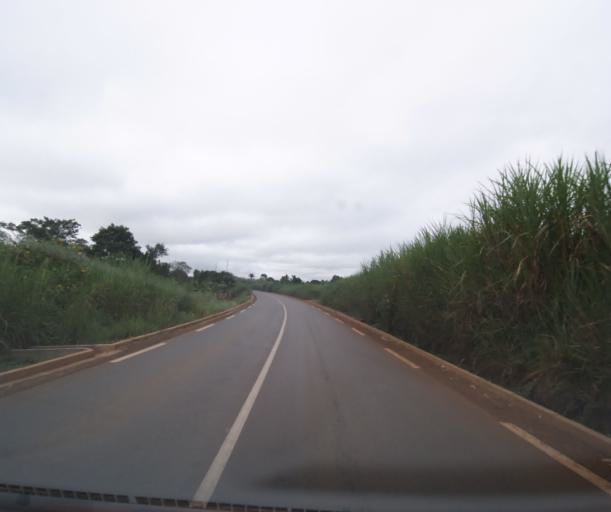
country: CM
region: West
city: Bansoa
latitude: 5.5402
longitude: 10.3270
